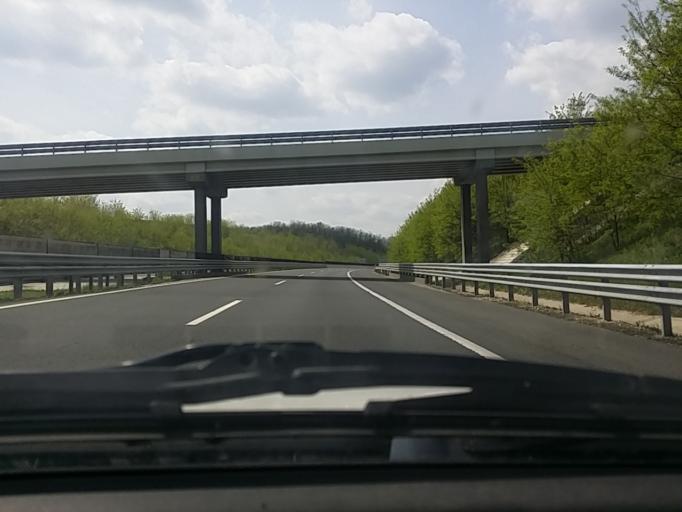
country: HU
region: Somogy
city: Balatonfoldvar
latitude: 46.8222
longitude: 17.9301
